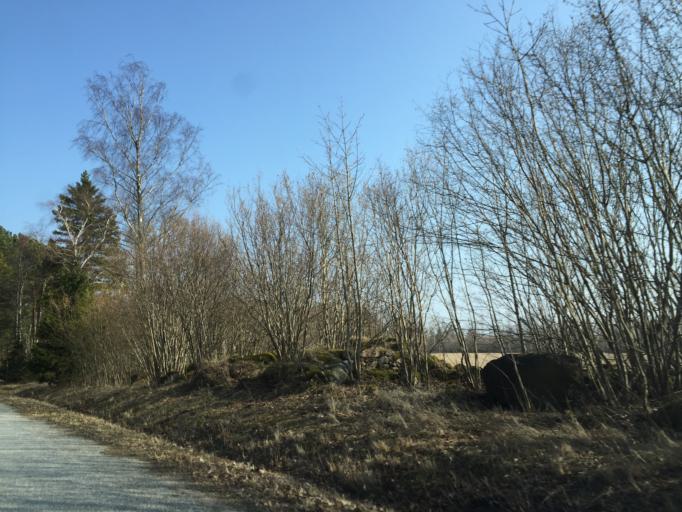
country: EE
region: Saare
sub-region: Orissaare vald
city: Orissaare
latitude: 58.5519
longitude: 23.2902
